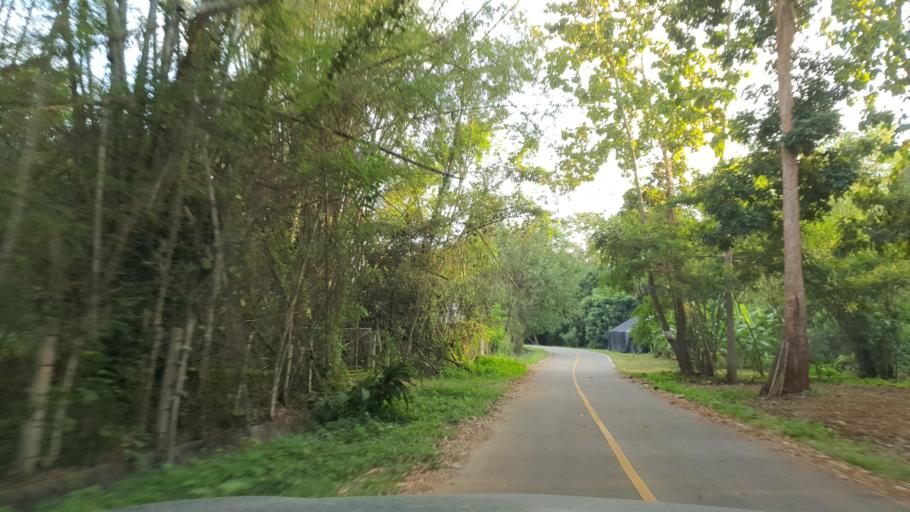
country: TH
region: Chiang Mai
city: Mae On
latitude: 18.8667
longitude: 99.2412
